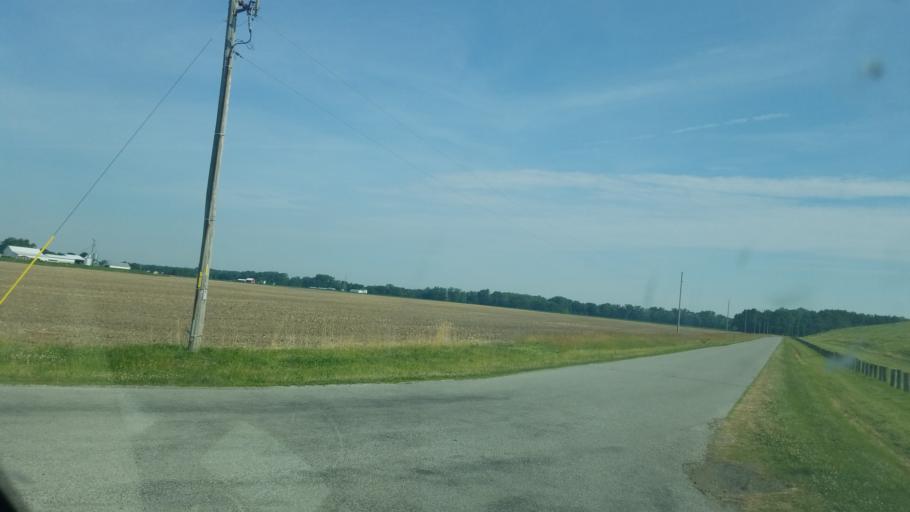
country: US
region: Ohio
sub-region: Hancock County
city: Findlay
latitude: 41.0219
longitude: -83.5807
